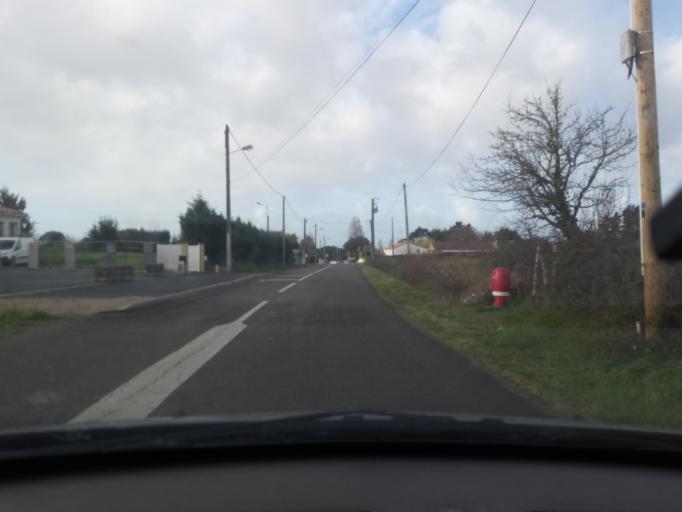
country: FR
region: Pays de la Loire
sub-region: Departement de la Vendee
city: Olonne-sur-Mer
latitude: 46.5680
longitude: -1.7665
